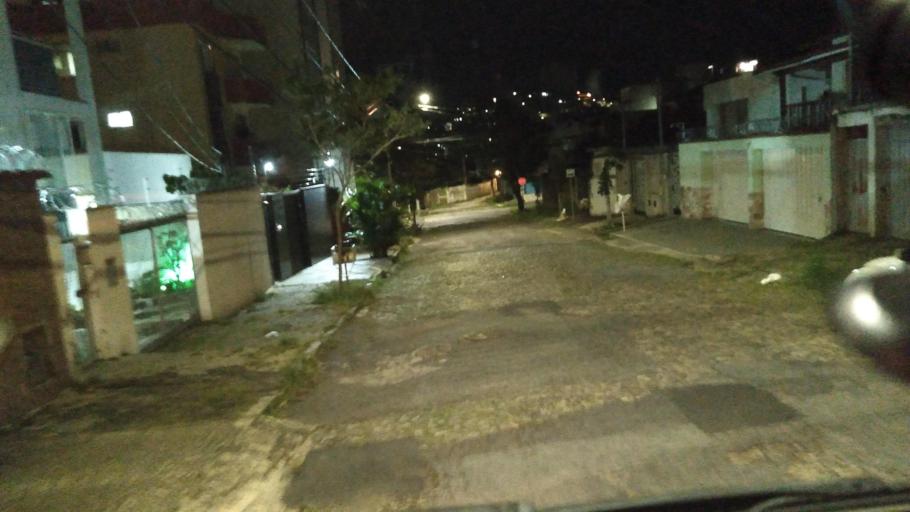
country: BR
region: Minas Gerais
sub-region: Belo Horizonte
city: Belo Horizonte
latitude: -19.9113
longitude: -43.9121
